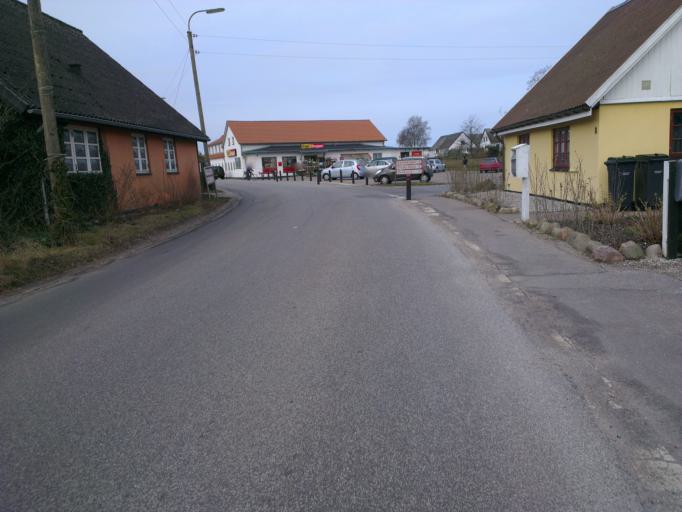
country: DK
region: Capital Region
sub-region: Frederikssund Kommune
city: Skibby
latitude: 55.7949
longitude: 11.9547
